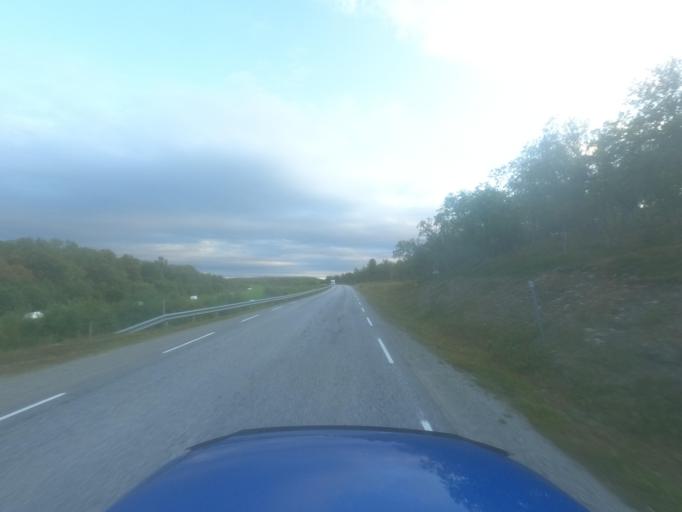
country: NO
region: Finnmark Fylke
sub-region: Porsanger
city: Lakselv
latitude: 70.2946
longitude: 25.0698
